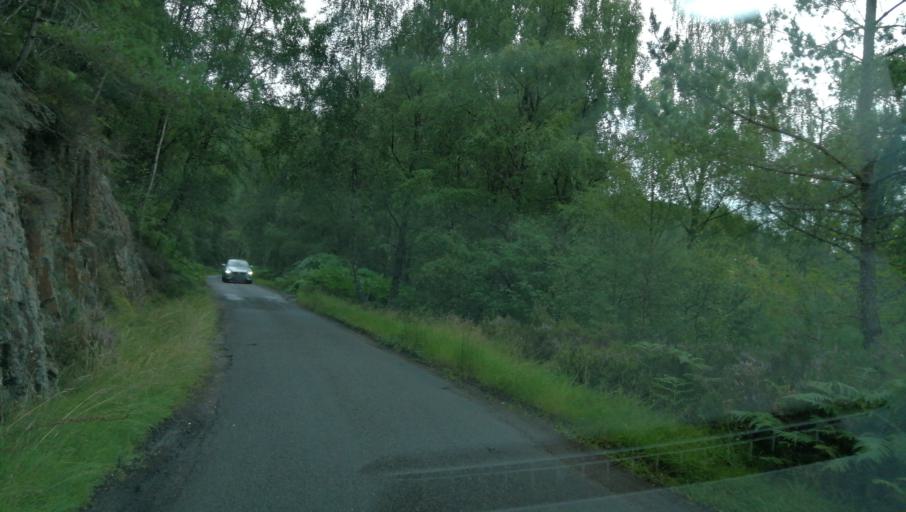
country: GB
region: Scotland
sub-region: Highland
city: Spean Bridge
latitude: 57.2992
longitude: -4.8984
